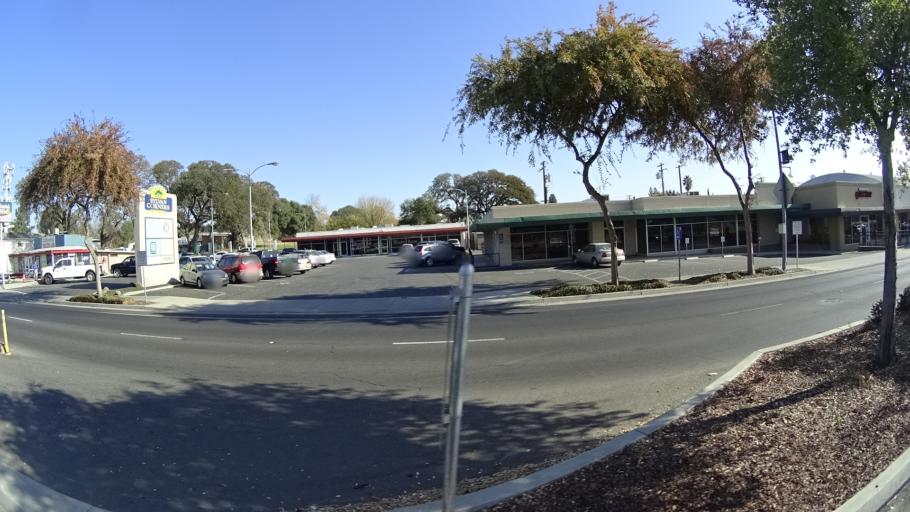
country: US
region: California
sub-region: Sacramento County
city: Citrus Heights
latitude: 38.6960
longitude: -121.2903
